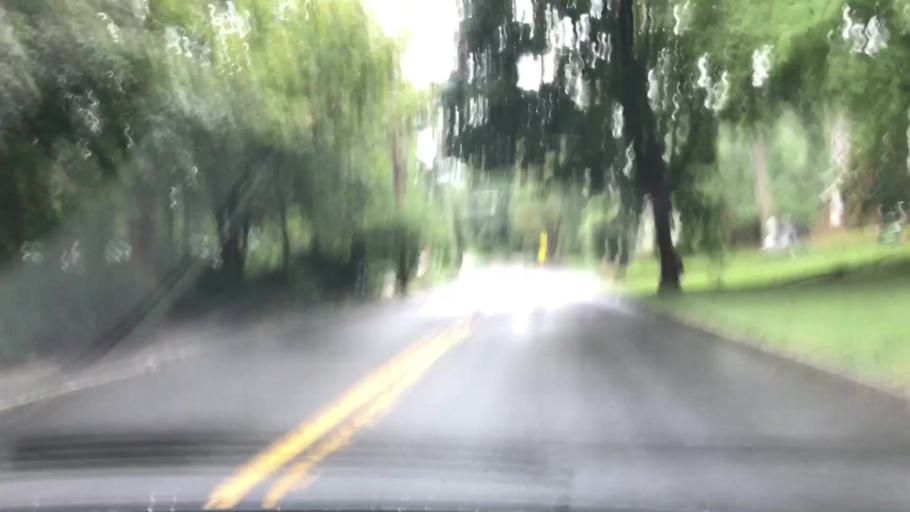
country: US
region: New Jersey
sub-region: Bergen County
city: Englewood
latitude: 40.9073
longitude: -73.9869
